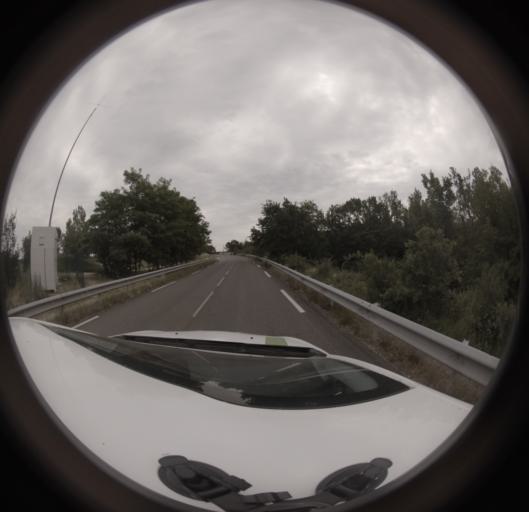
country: FR
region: Midi-Pyrenees
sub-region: Departement du Tarn-et-Garonne
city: Montauban
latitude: 44.0026
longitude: 1.3791
